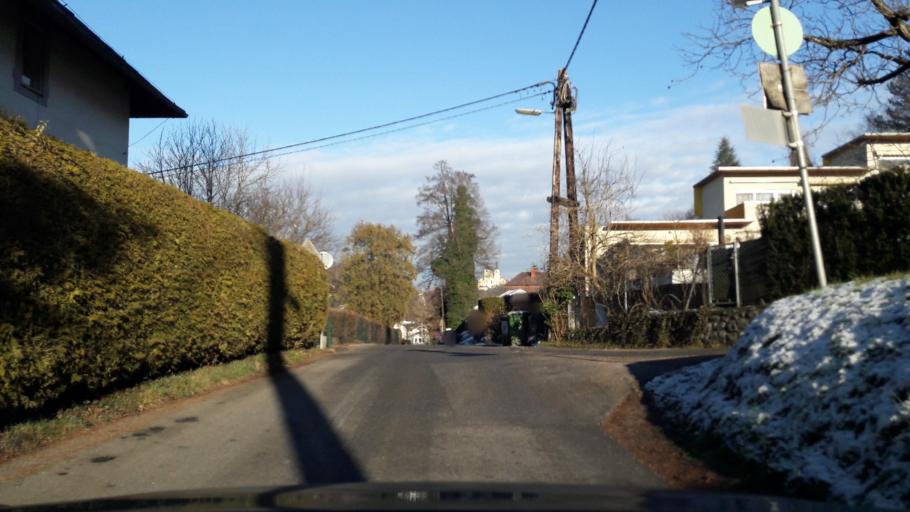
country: AT
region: Styria
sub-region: Graz Stadt
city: Mariatrost
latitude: 47.0979
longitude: 15.4774
